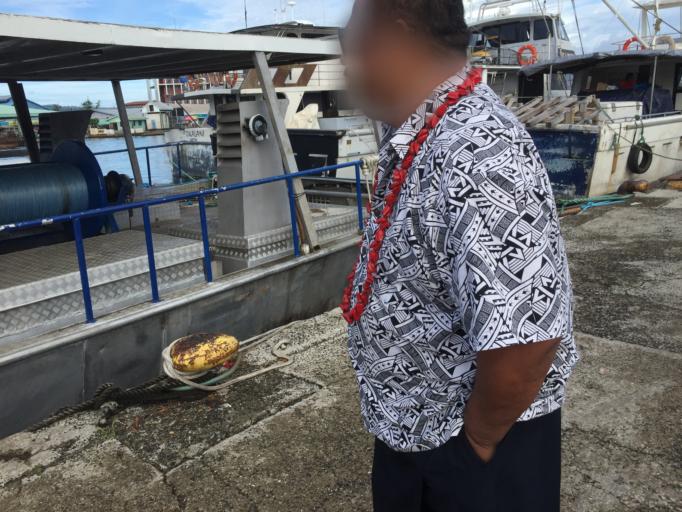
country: WS
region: Tuamasaga
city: Apia
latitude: -13.8289
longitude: -171.7693
